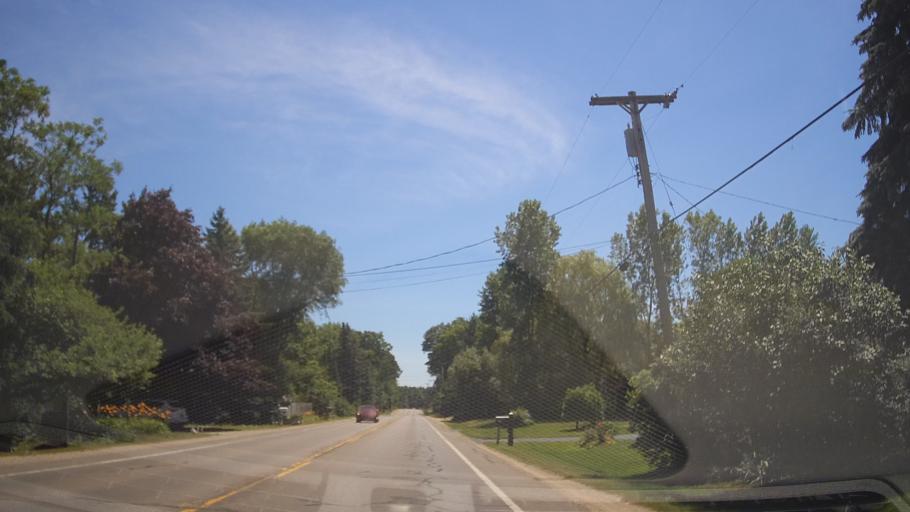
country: US
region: Michigan
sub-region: Grand Traverse County
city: Traverse City
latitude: 44.6921
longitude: -85.6908
